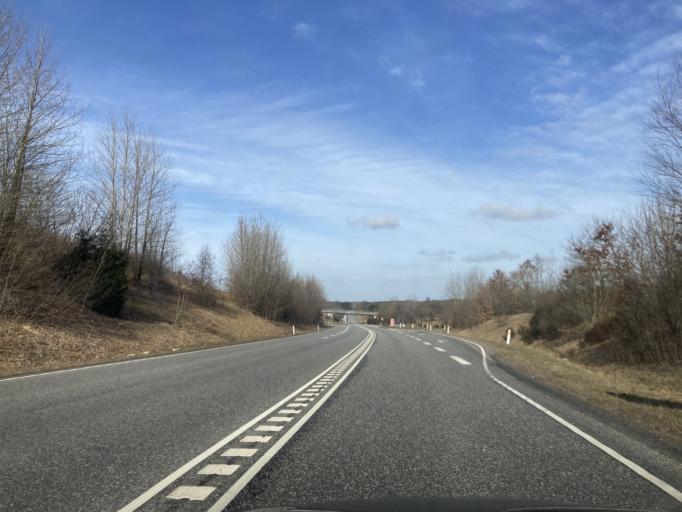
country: DK
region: Central Jutland
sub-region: Hedensted Kommune
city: Torring
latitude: 55.9666
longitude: 9.4046
